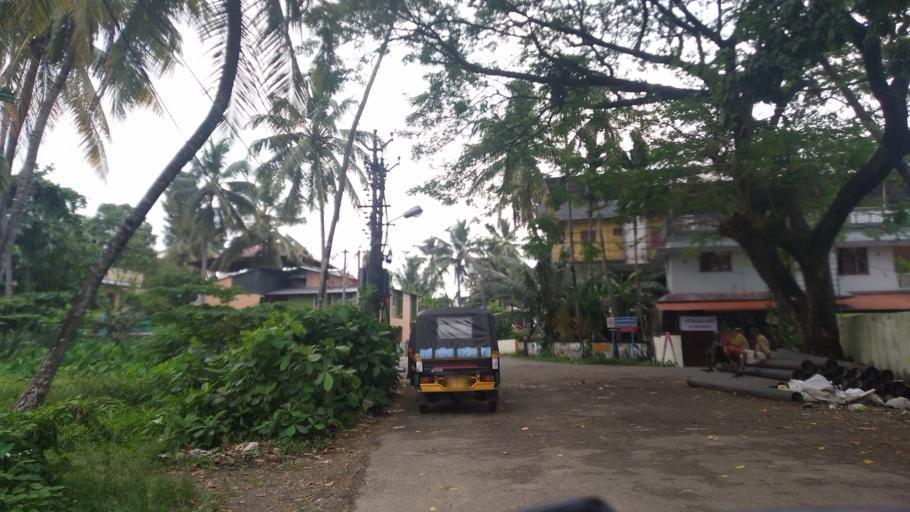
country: IN
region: Kerala
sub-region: Ernakulam
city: Cochin
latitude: 9.9783
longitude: 76.3027
